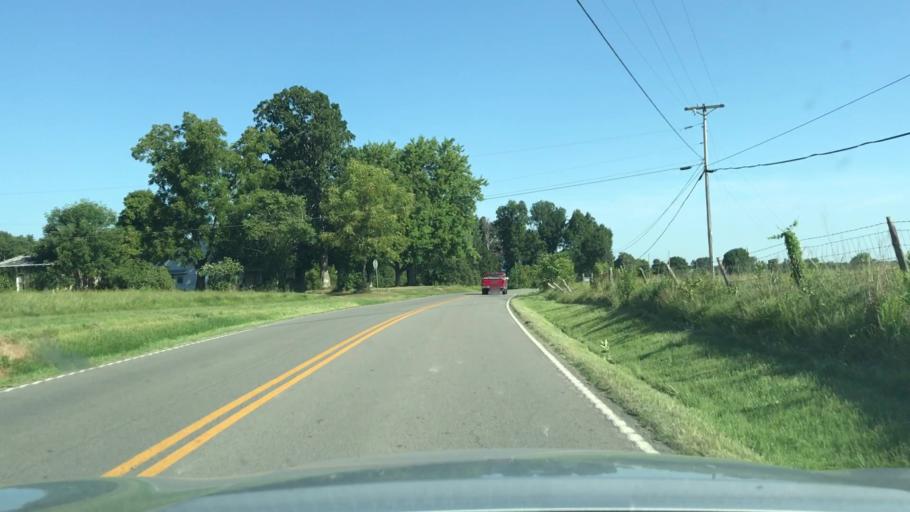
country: US
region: Kentucky
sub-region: Muhlenberg County
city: Greenville
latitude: 37.1720
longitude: -87.1518
